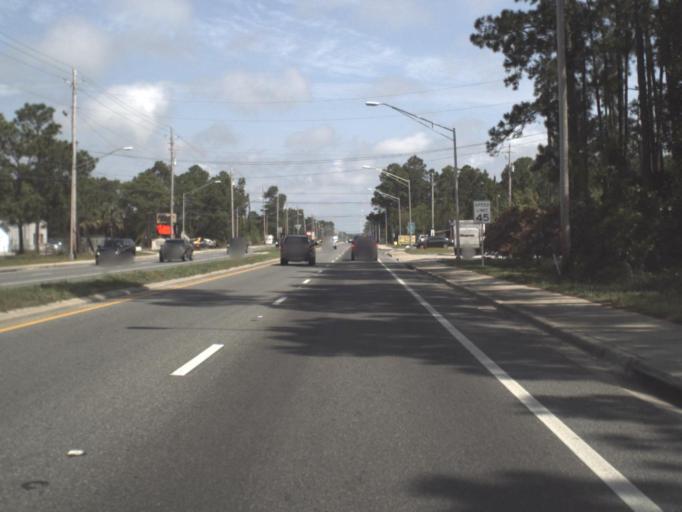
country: US
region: Florida
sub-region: Santa Rosa County
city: Navarre
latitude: 30.4122
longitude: -86.8697
